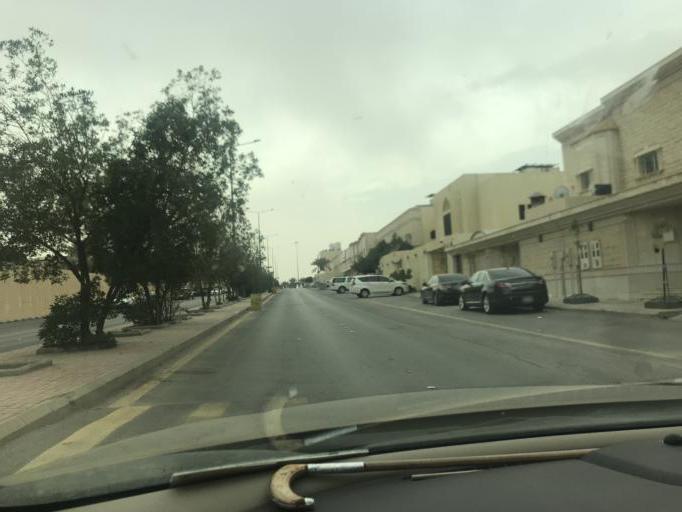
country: SA
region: Ar Riyad
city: Riyadh
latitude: 24.7367
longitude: 46.7543
